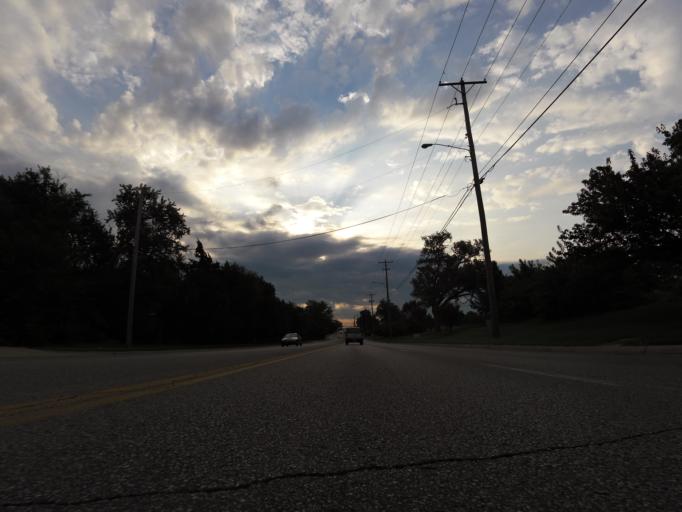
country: US
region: Kansas
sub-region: Sedgwick County
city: Bellaire
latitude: 37.7228
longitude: -97.2857
